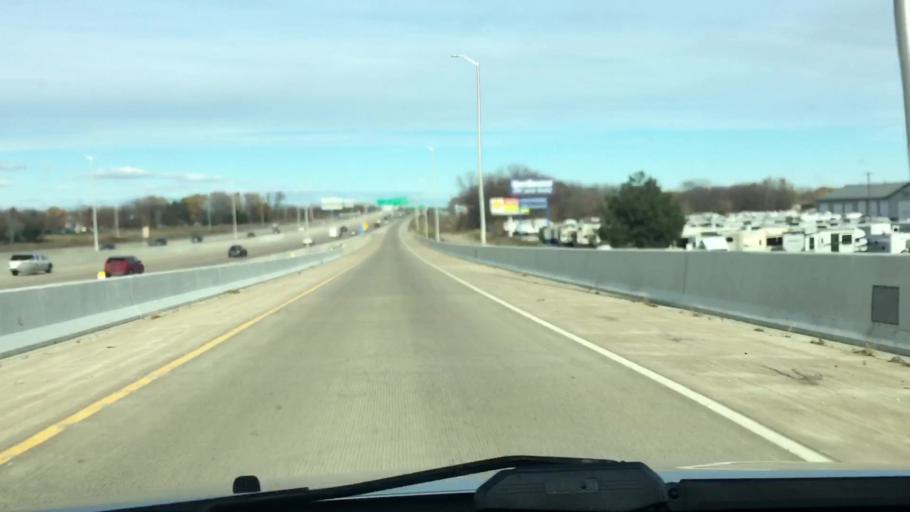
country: US
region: Wisconsin
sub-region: Brown County
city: Howard
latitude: 44.5423
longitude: -88.0733
